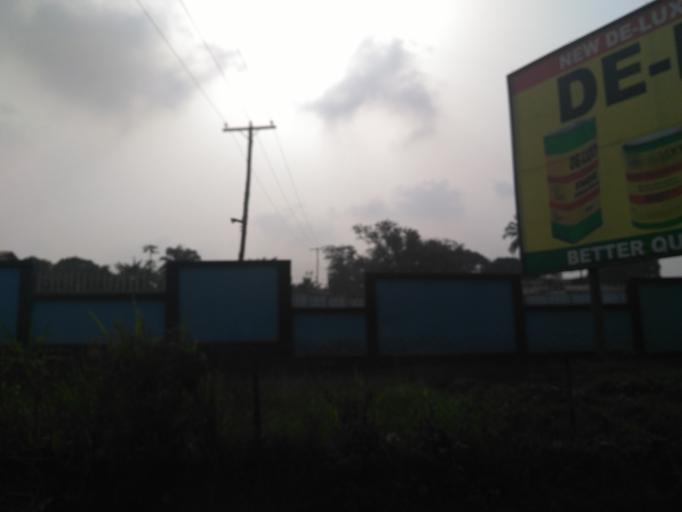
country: GH
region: Ashanti
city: Kumasi
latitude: 6.6922
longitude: -1.5949
